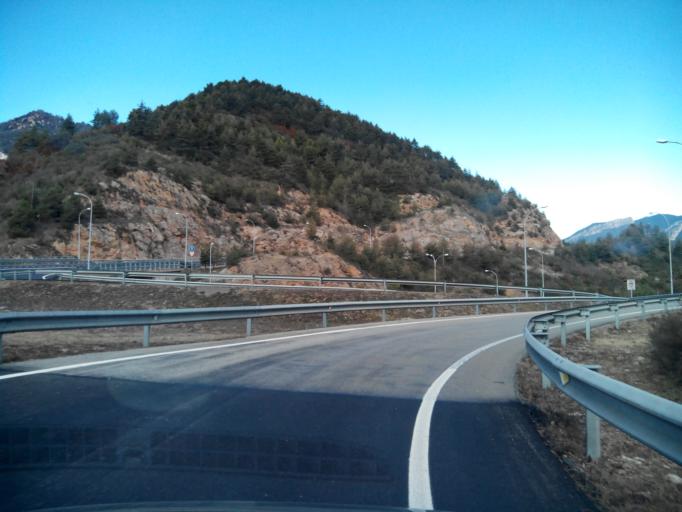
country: ES
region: Catalonia
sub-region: Provincia de Barcelona
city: Berga
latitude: 42.1129
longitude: 1.8607
